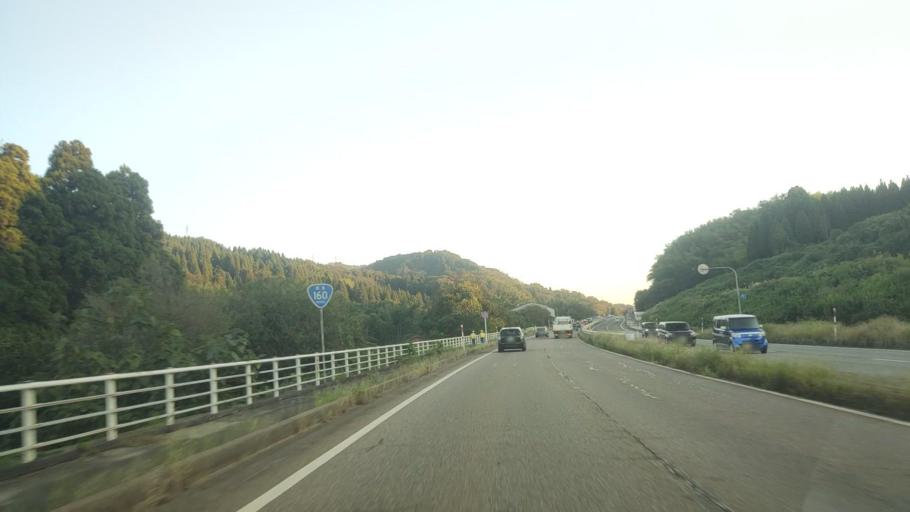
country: JP
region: Toyama
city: Himi
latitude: 36.8023
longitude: 137.0014
